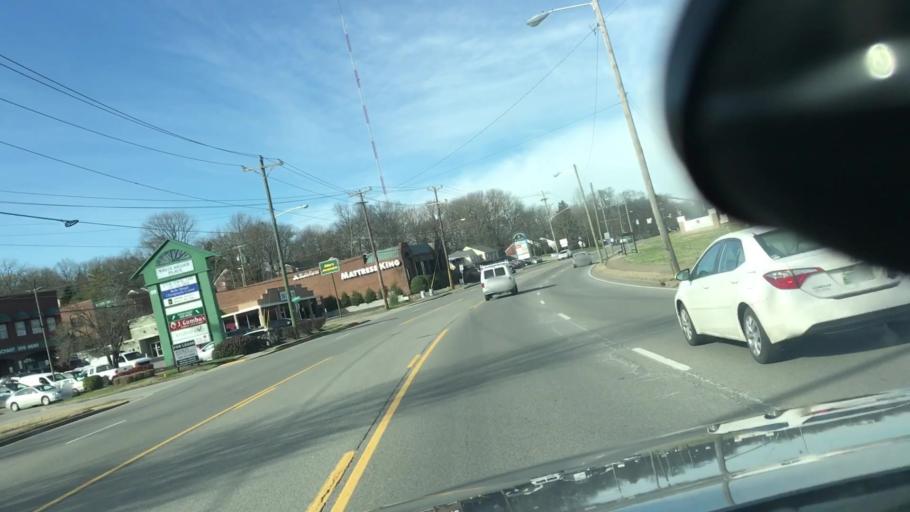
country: US
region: Tennessee
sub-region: Davidson County
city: Belle Meade
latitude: 36.1314
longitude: -86.8572
